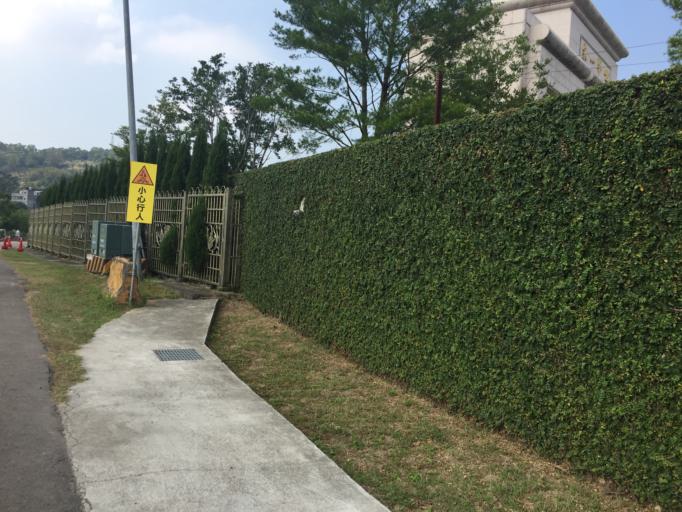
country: TW
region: Taiwan
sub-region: Hsinchu
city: Hsinchu
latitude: 24.6809
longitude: 120.9832
